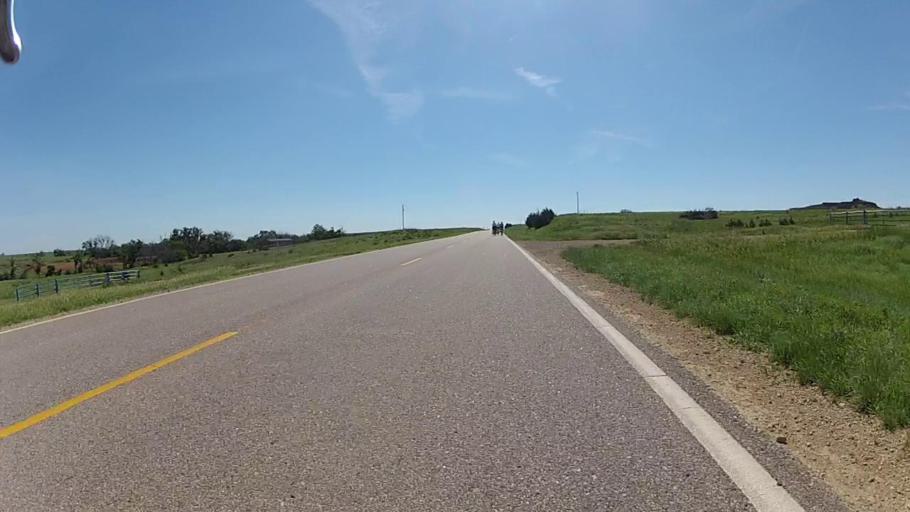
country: US
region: Kansas
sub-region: Barber County
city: Medicine Lodge
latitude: 37.2753
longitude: -98.7131
